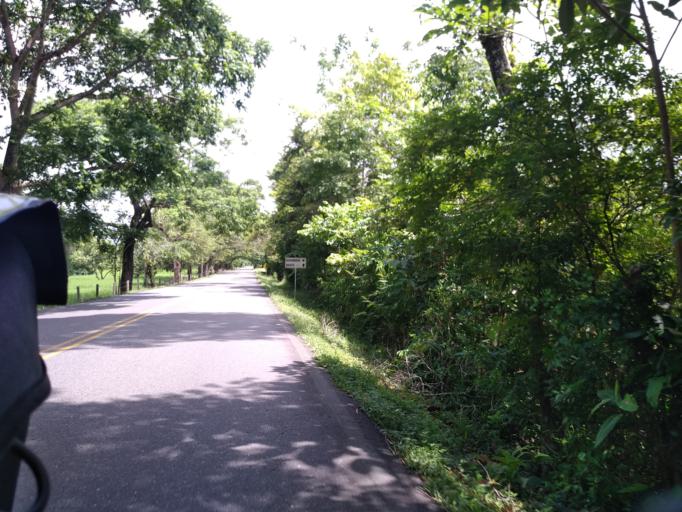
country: CO
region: Santander
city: Puerto Parra
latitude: 6.5211
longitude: -74.0803
